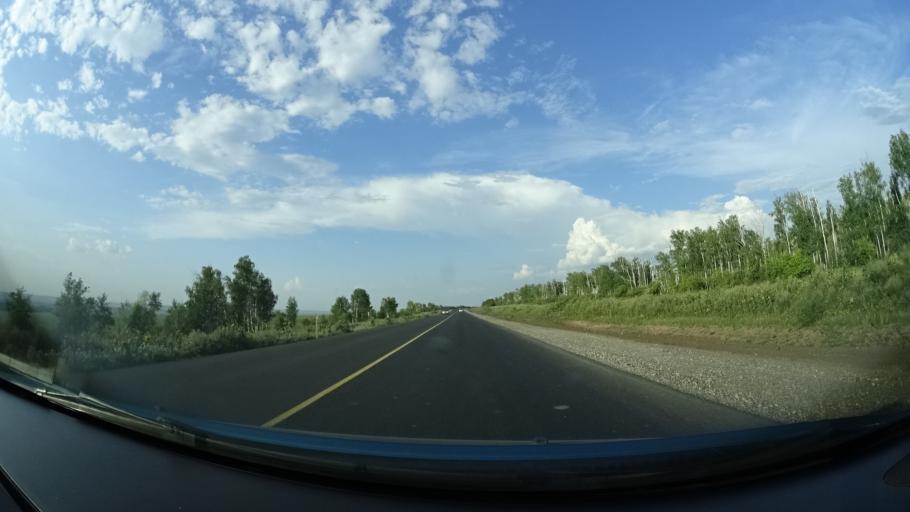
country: RU
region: Samara
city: Sukhodol
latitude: 53.7653
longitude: 50.8874
